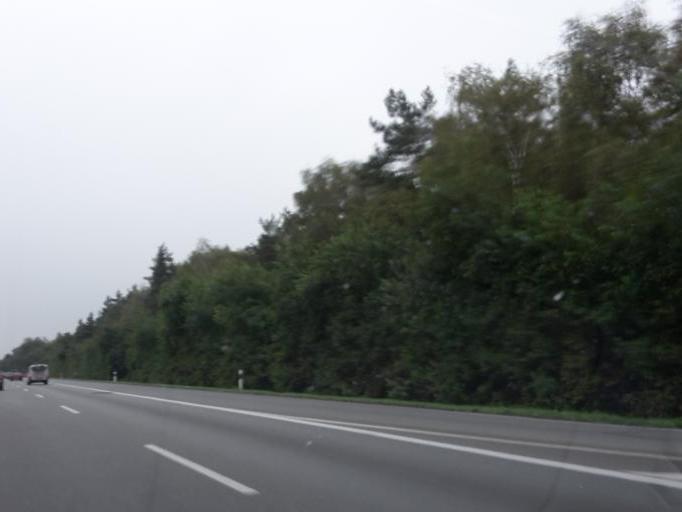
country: DE
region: Lower Saxony
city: Rieste
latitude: 52.4689
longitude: 8.0527
